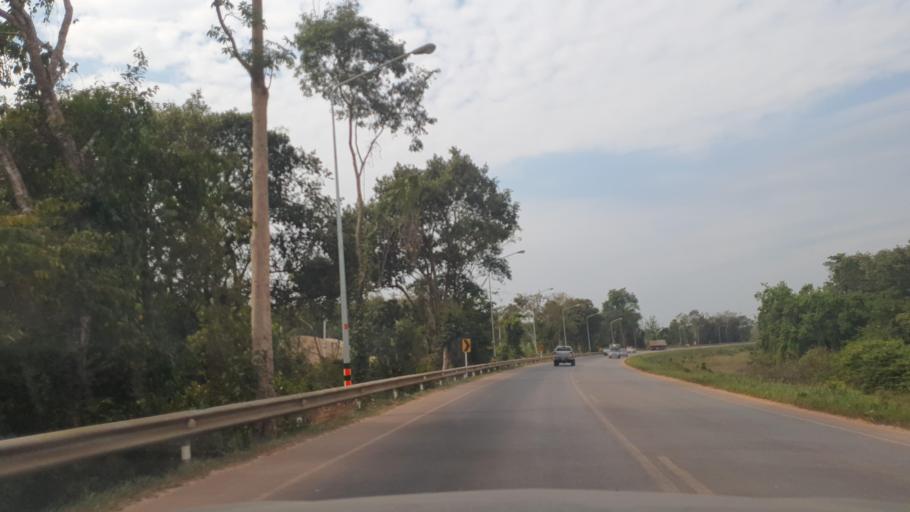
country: TH
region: Changwat Bueng Kan
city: Si Wilai
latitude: 18.2718
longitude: 103.8382
